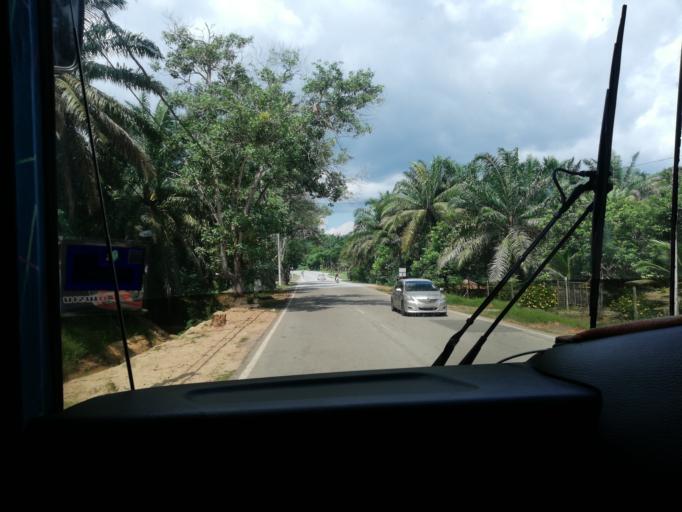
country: MY
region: Perak
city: Parit Buntar
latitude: 5.1200
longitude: 100.5646
